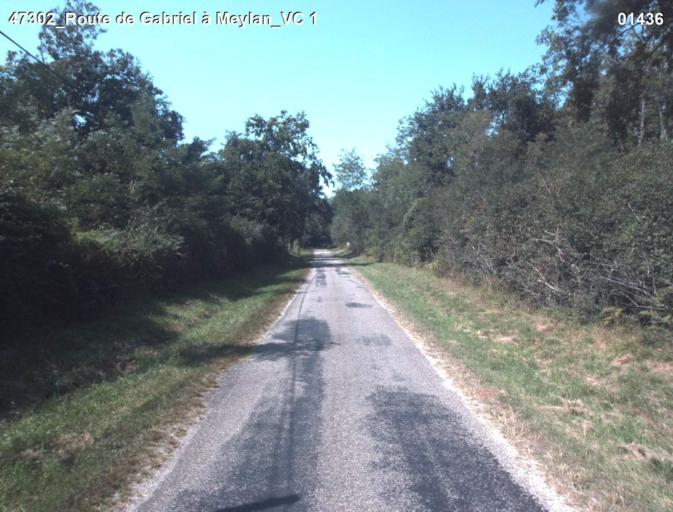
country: FR
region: Aquitaine
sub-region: Departement du Lot-et-Garonne
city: Mezin
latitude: 44.0643
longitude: 0.1417
